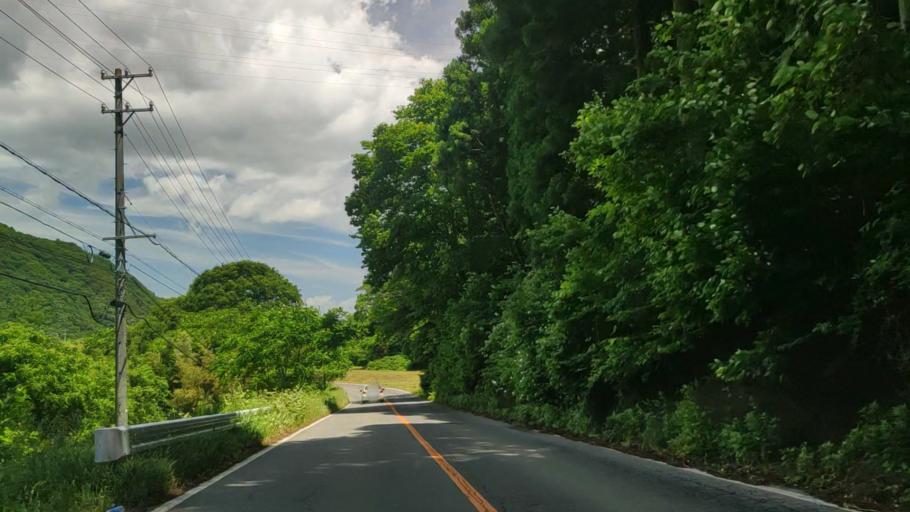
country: JP
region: Nagano
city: Kamimaruko
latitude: 36.2098
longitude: 138.2472
